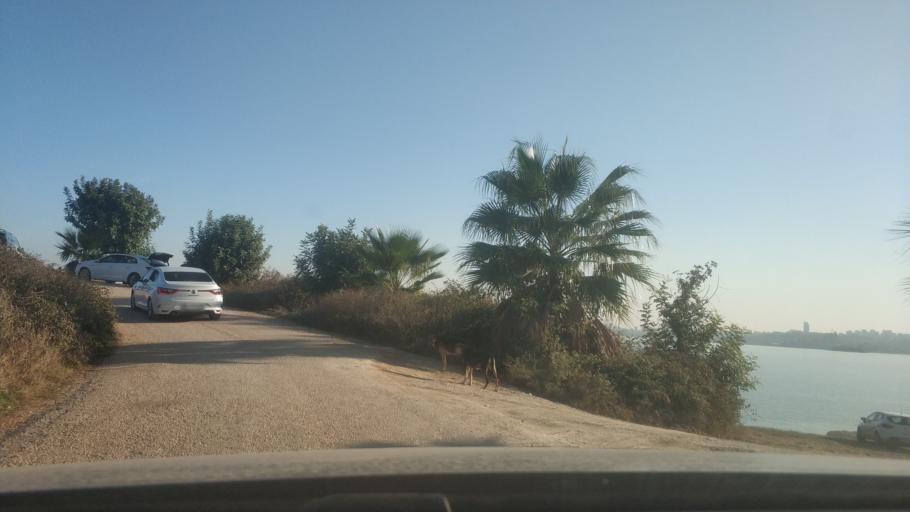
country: TR
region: Adana
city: Adana
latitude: 37.0903
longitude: 35.3014
